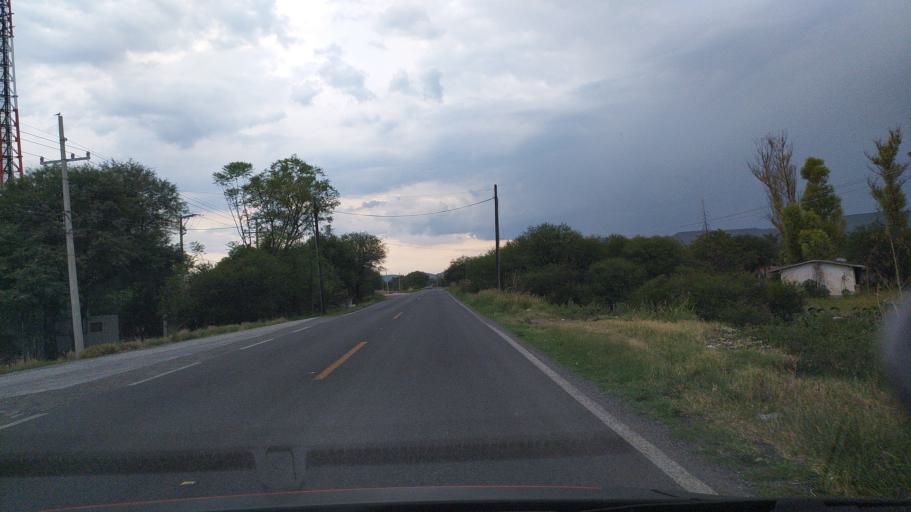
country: MX
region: Guanajuato
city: San Roque
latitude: 20.9715
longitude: -101.8587
